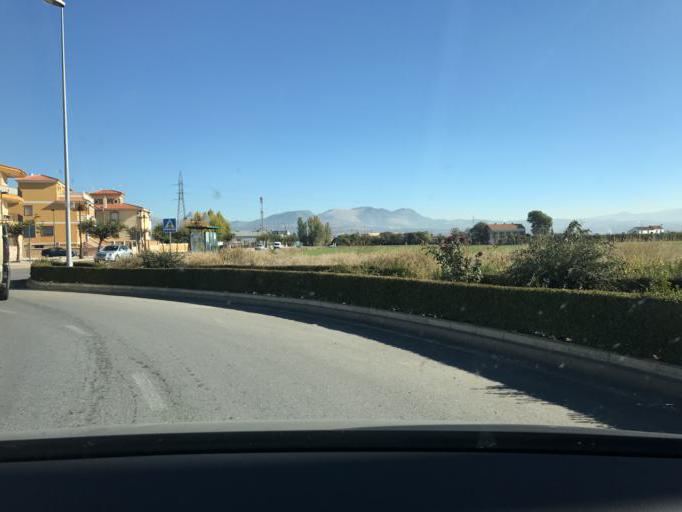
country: ES
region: Andalusia
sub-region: Provincia de Granada
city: Atarfe
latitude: 37.2249
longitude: -3.6767
